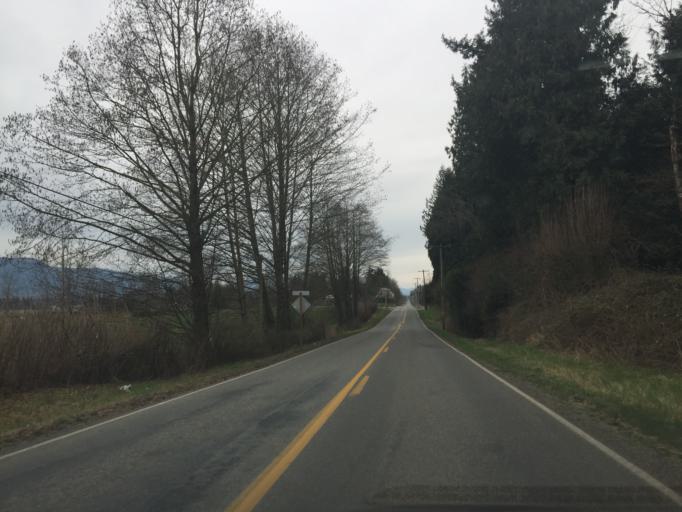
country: US
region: Washington
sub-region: Whatcom County
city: Nooksack
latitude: 48.9778
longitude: -122.3311
